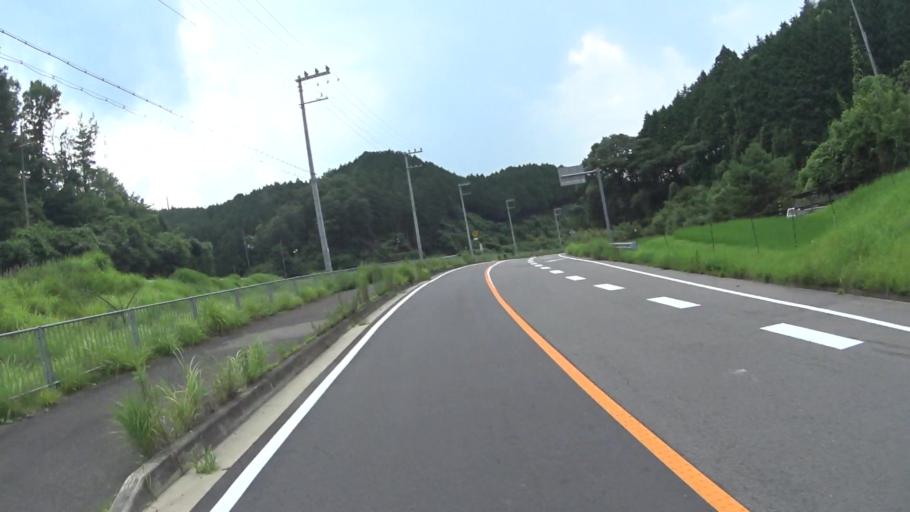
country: JP
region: Kyoto
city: Yawata
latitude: 34.8744
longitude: 135.7465
